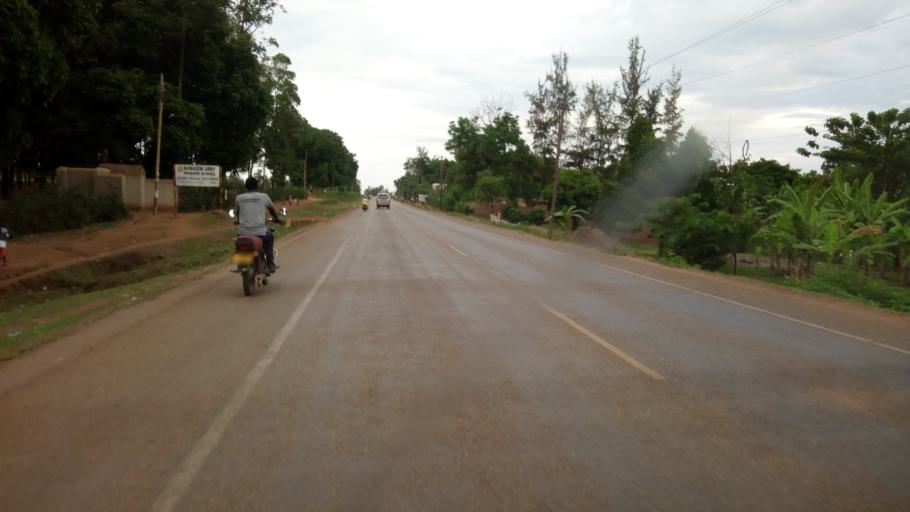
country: UG
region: Eastern Region
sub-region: Mbale District
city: Mbale
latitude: 1.0355
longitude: 34.1773
